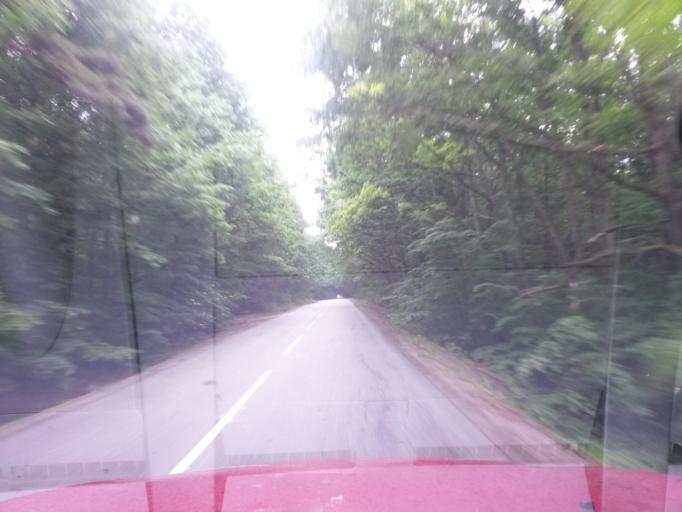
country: SK
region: Kosicky
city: Kosice
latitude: 48.7143
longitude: 21.1877
